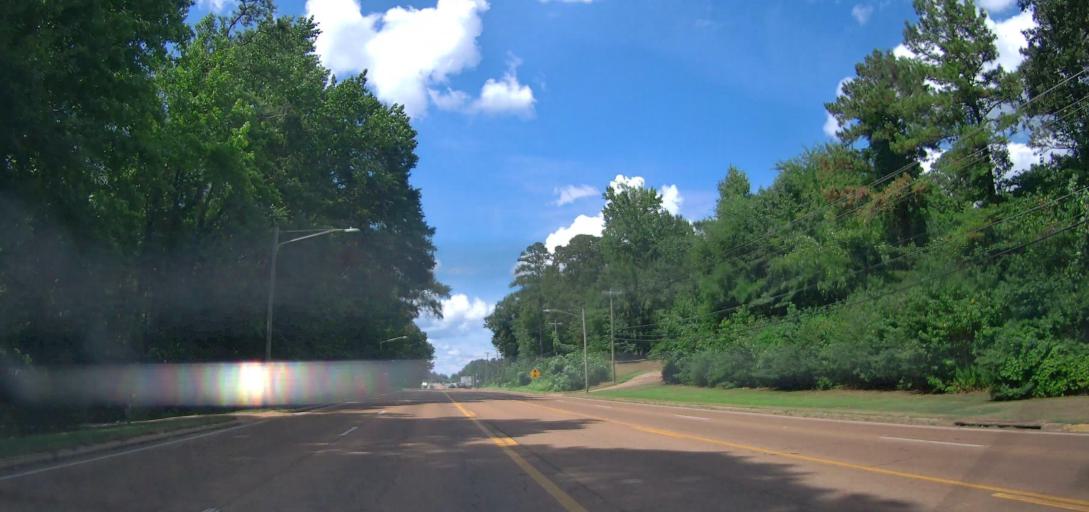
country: US
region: Mississippi
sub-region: Lowndes County
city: Columbus
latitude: 33.5534
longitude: -88.4332
